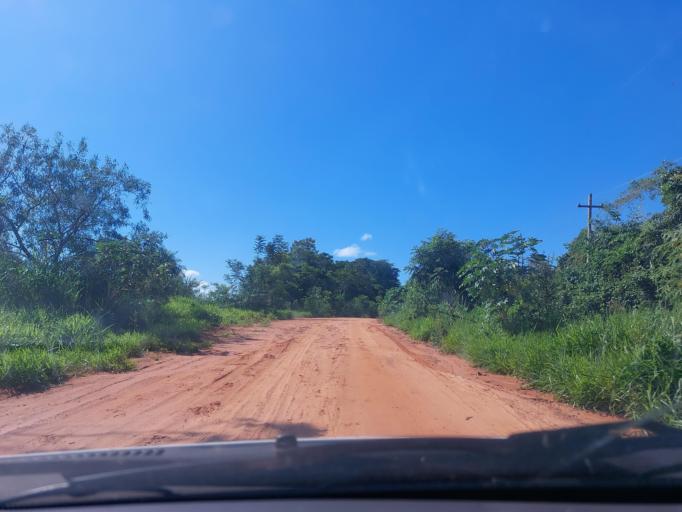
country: PY
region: San Pedro
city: Itacurubi del Rosario
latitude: -24.5420
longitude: -56.5836
